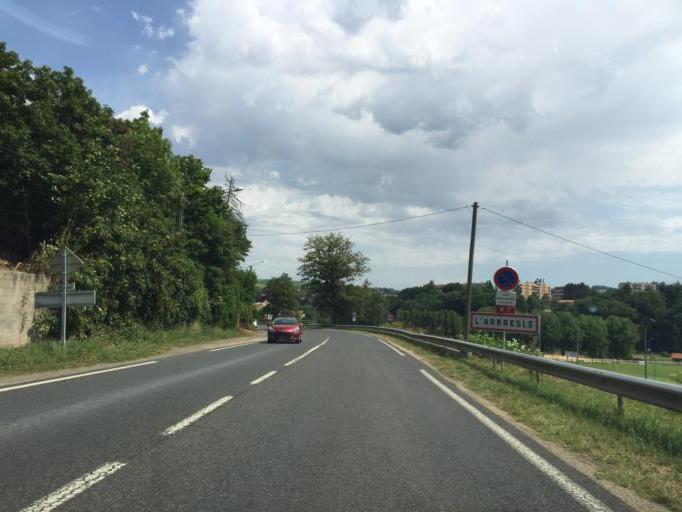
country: FR
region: Rhone-Alpes
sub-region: Departement du Rhone
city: Saint-Germain-Nuelles
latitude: 45.8389
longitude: 4.6062
